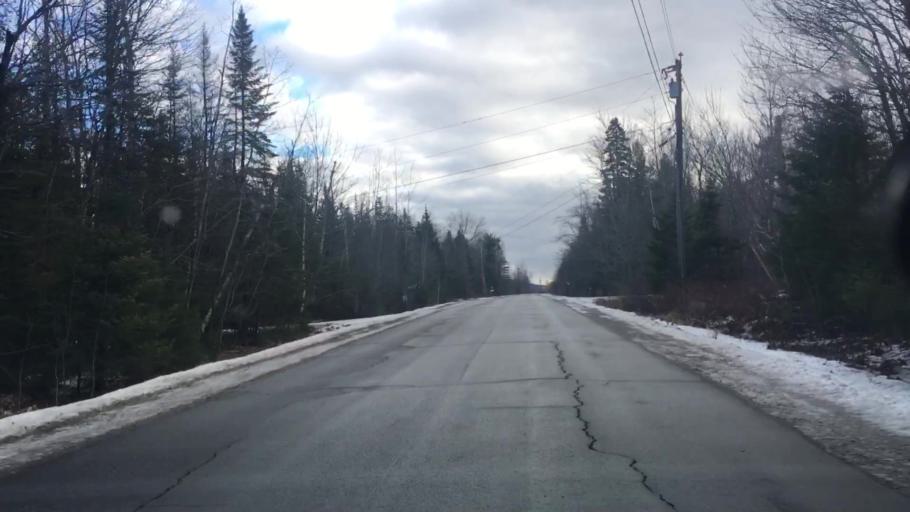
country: US
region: Maine
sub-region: Hancock County
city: Dedham
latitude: 44.6781
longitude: -68.7037
